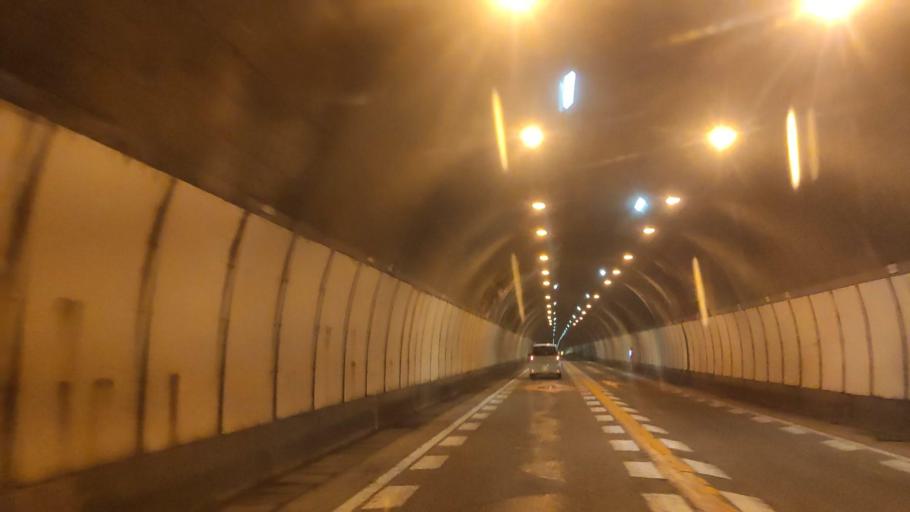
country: JP
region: Hyogo
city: Toyooka
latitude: 35.4824
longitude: 134.5827
